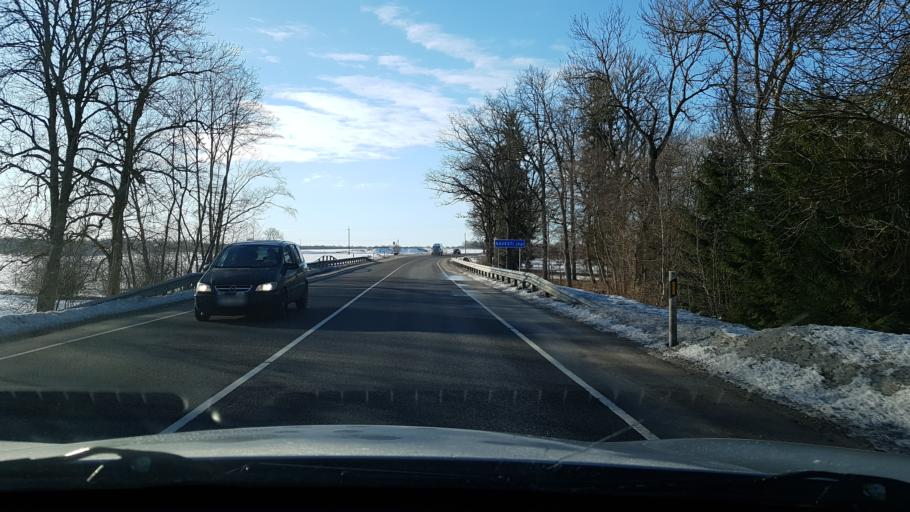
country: EE
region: Viljandimaa
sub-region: Vohma linn
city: Vohma
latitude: 58.7145
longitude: 25.7527
